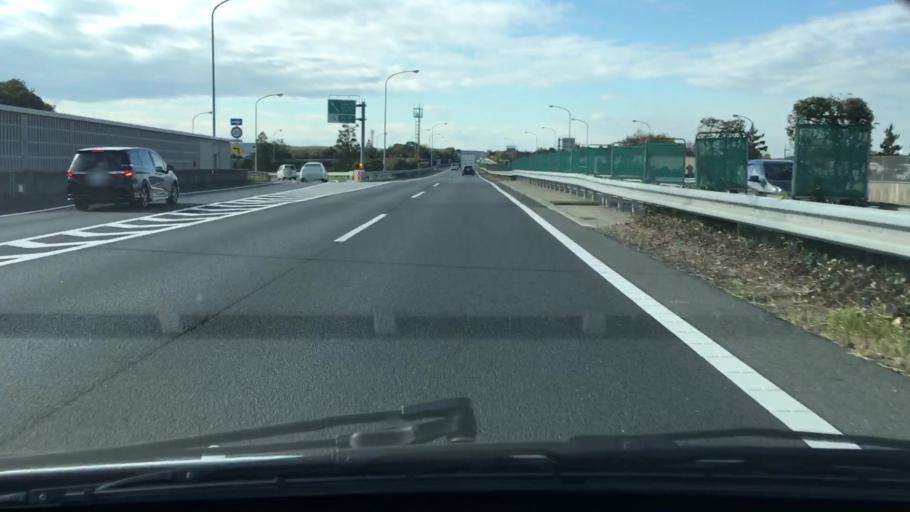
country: JP
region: Chiba
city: Ichihara
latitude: 35.4964
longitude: 140.0938
